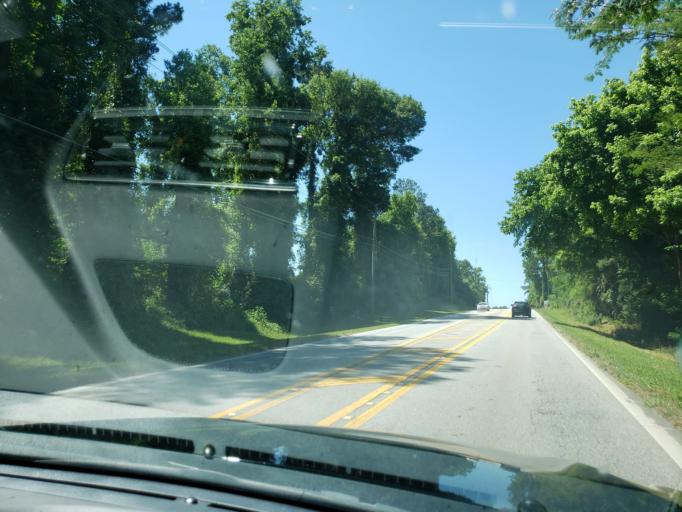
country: US
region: Alabama
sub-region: Lee County
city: Auburn
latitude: 32.6418
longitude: -85.4814
